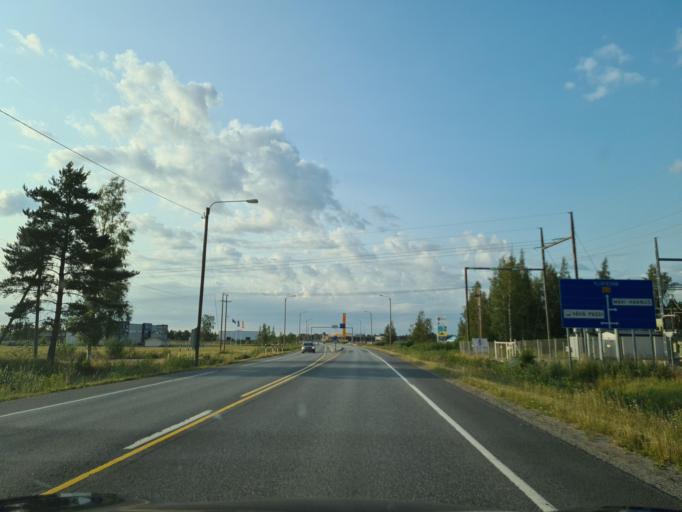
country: FI
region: Southern Ostrobothnia
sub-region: Seinaejoki
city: Kauhava
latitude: 63.0853
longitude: 23.0591
